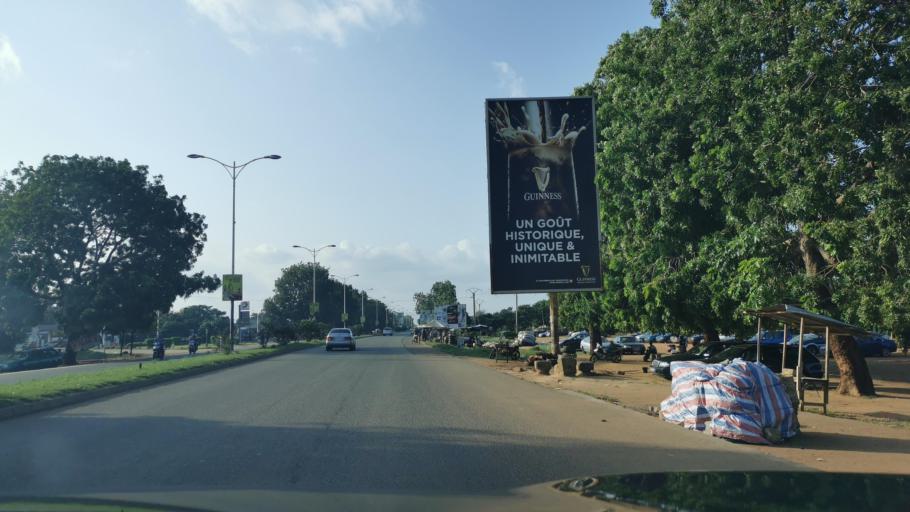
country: TG
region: Maritime
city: Lome
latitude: 6.2010
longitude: 1.2086
